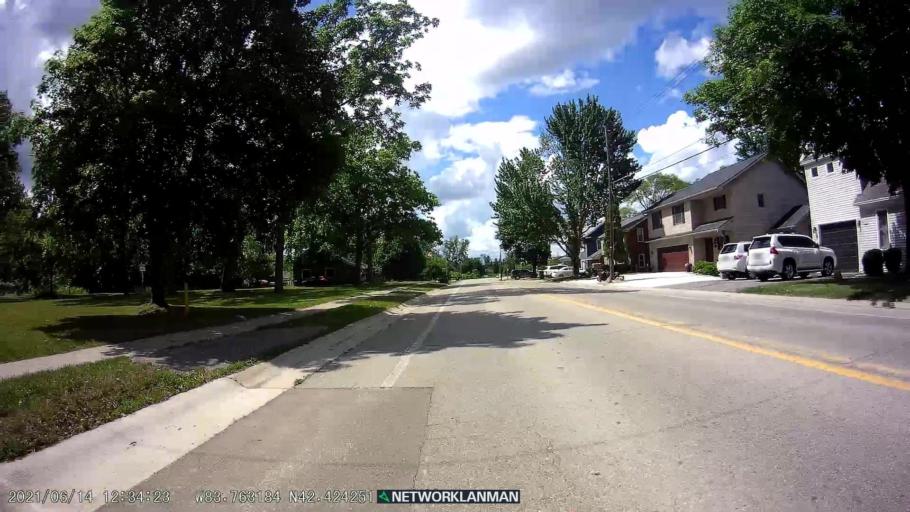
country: US
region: Michigan
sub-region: Livingston County
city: Whitmore Lake
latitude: 42.4242
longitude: -83.7632
